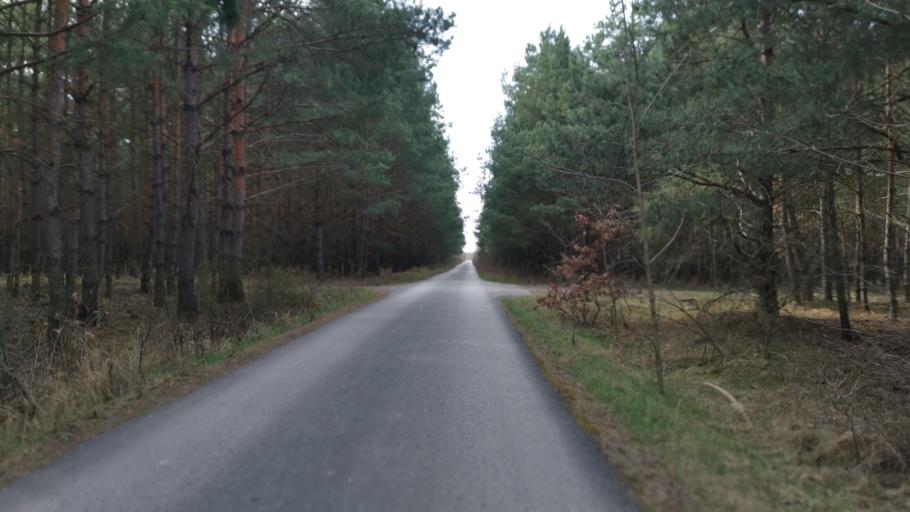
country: SK
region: Trnavsky
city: Gbely
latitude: 48.6924
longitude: 17.0414
